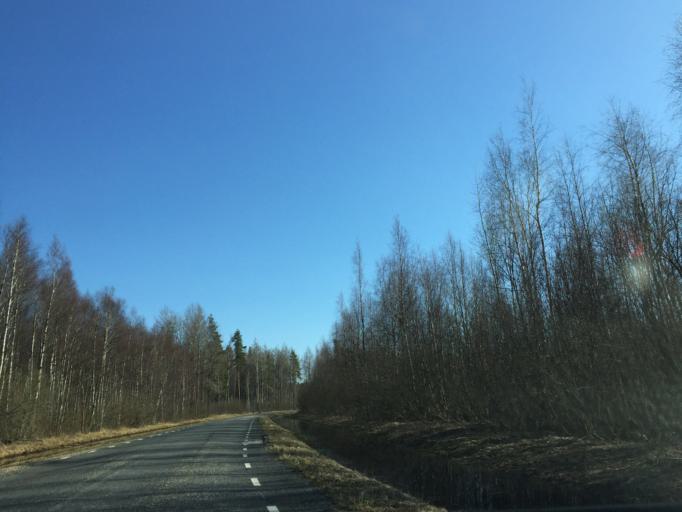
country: RU
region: Pskov
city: Gdov
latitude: 59.0053
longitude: 27.6926
